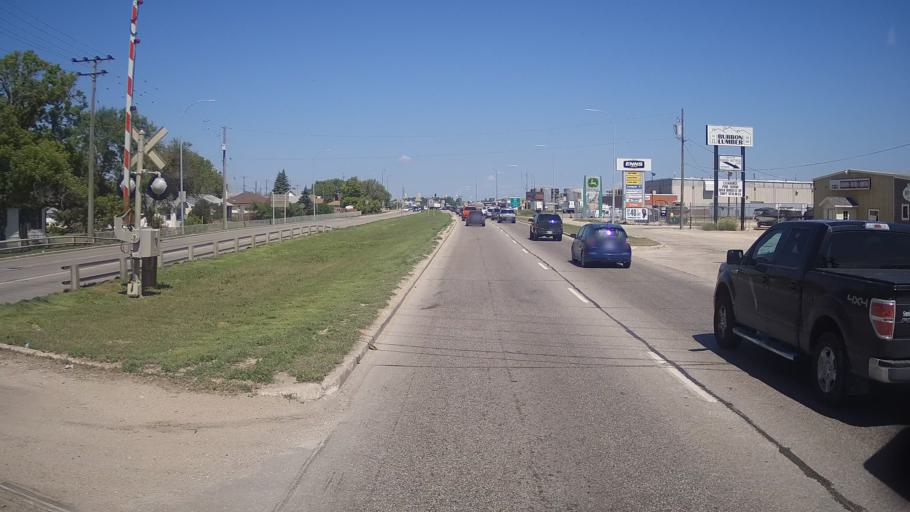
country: CA
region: Manitoba
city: Winnipeg
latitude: 49.8829
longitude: -97.0721
